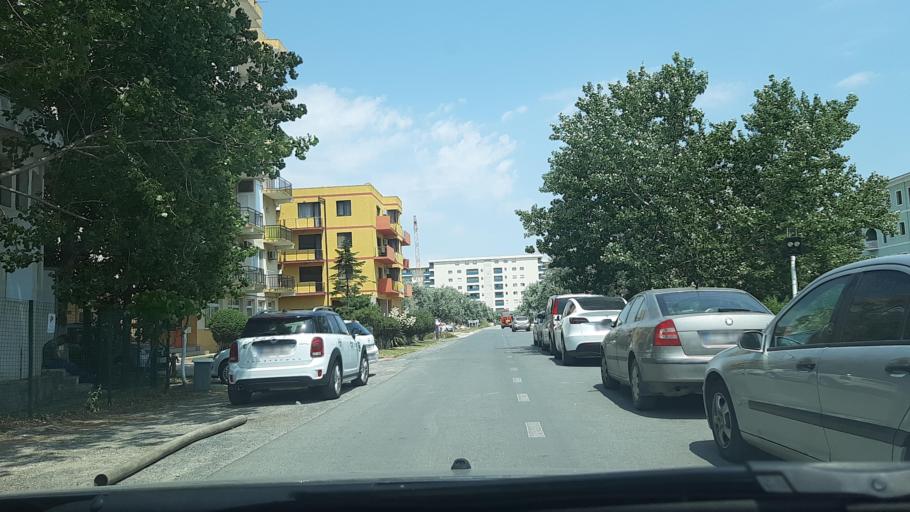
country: RO
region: Constanta
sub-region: Comuna Navodari
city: Navodari
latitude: 44.2810
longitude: 28.6197
